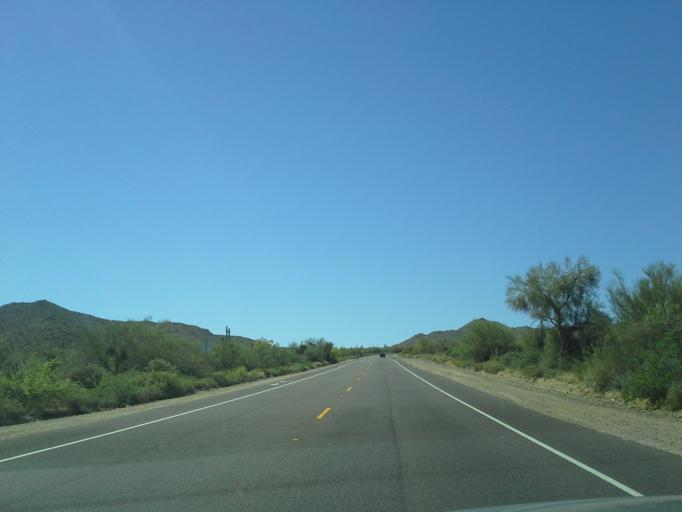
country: US
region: Arizona
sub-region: Maricopa County
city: Fountain Hills
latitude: 33.5344
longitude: -111.6110
